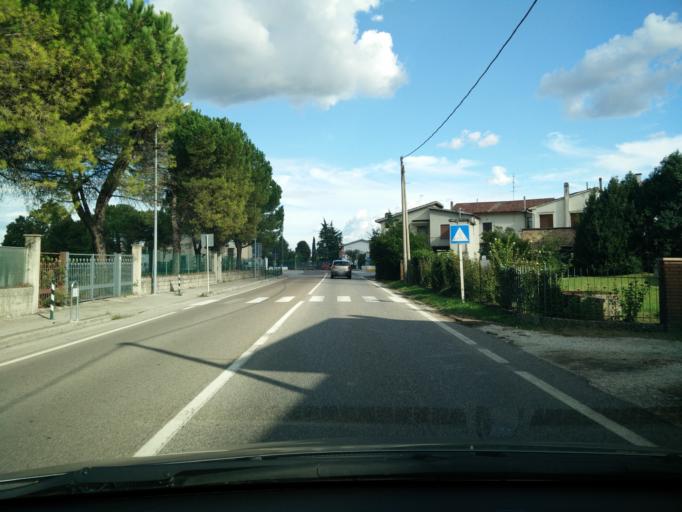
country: IT
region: Veneto
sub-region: Provincia di Treviso
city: Lancenigo-Villorba
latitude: 45.7362
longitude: 12.2652
